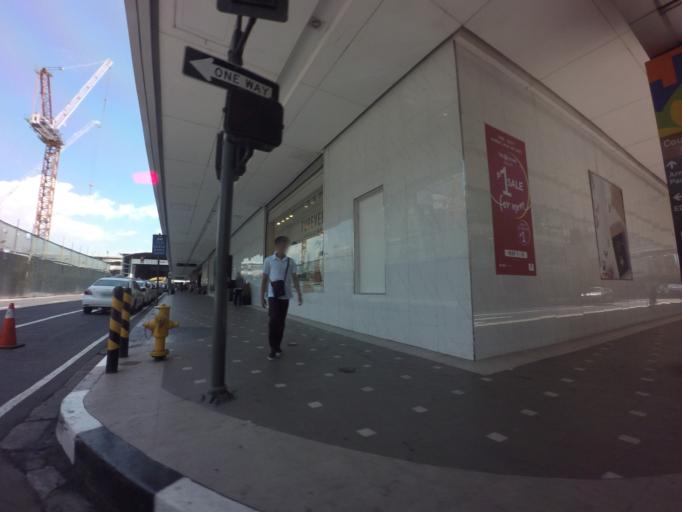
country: PH
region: Metro Manila
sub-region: Makati City
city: Makati City
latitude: 14.5505
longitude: 121.0265
